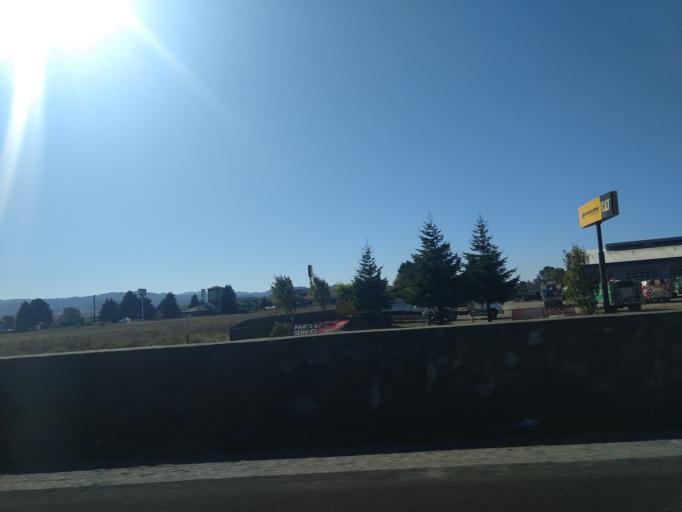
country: US
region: California
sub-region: Humboldt County
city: Fortuna
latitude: 40.5796
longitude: -124.1503
